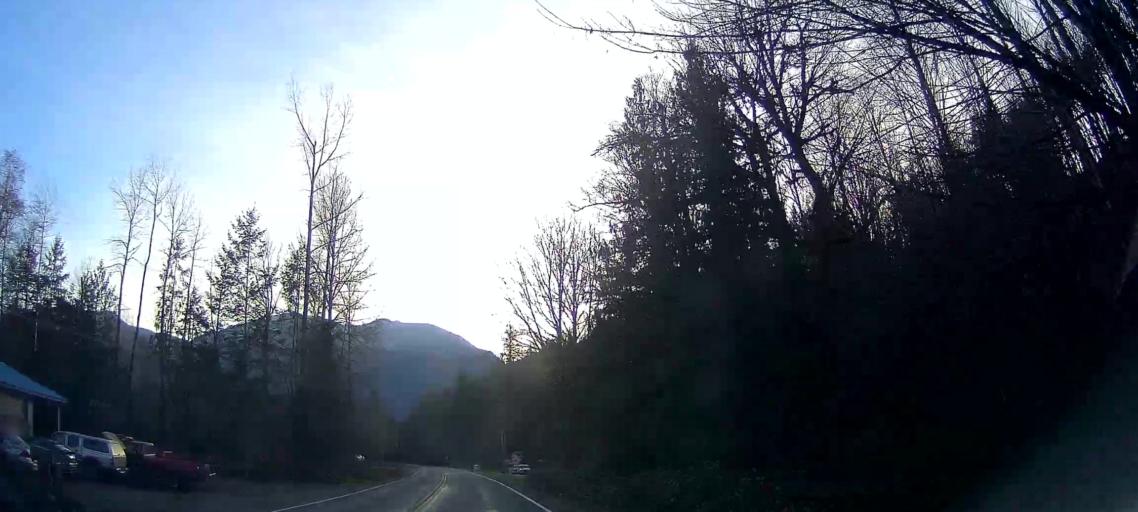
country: US
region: Washington
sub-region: Skagit County
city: Sedro-Woolley
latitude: 48.5389
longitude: -121.8841
